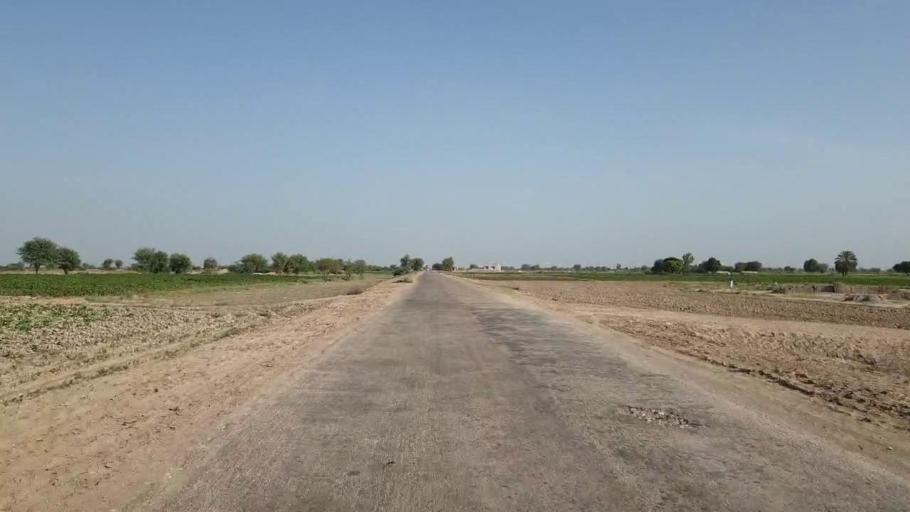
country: PK
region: Sindh
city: Nawabshah
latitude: 26.1452
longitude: 68.4502
